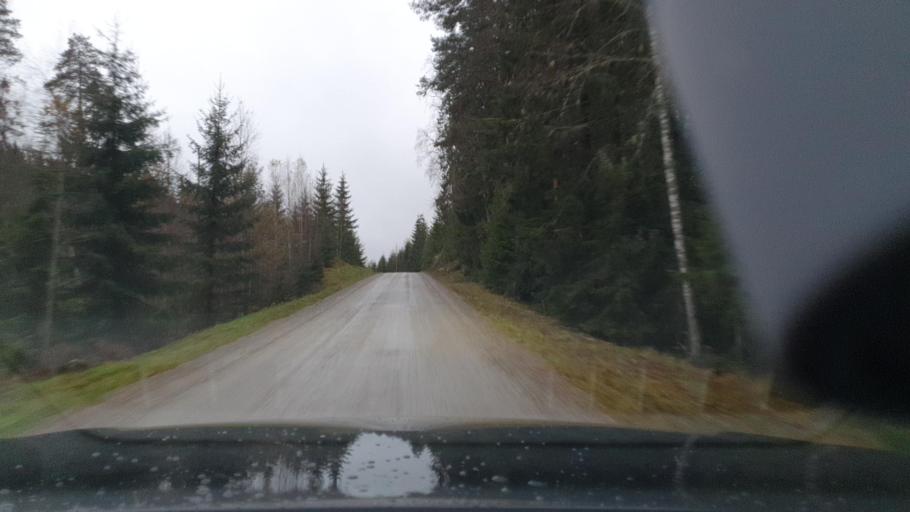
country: SE
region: Vaermland
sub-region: Arvika Kommun
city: Arvika
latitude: 59.8240
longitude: 12.7439
